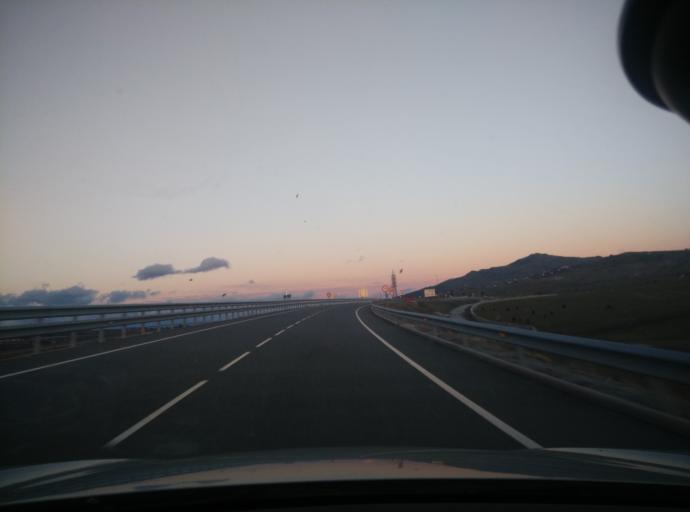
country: ES
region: Madrid
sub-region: Provincia de Madrid
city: Colmenar Viejo
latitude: 40.7266
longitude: -3.7869
